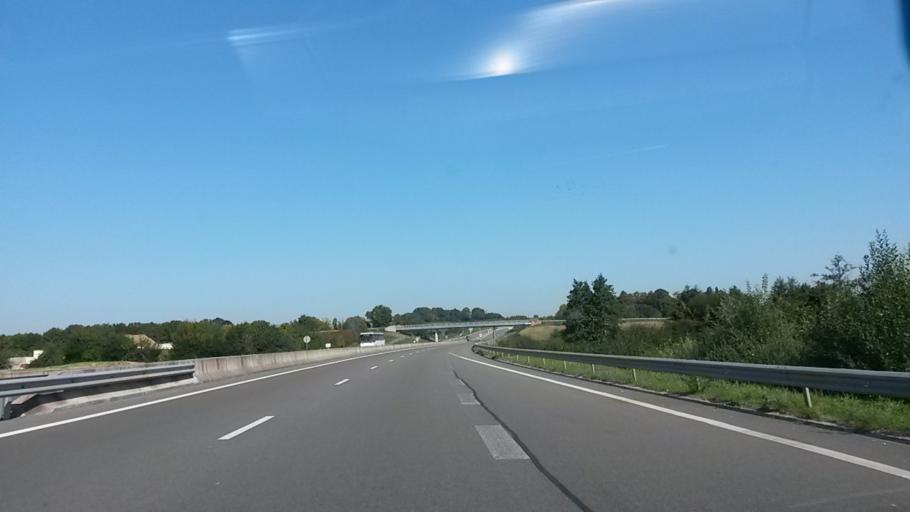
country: FR
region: Nord-Pas-de-Calais
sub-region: Departement du Nord
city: Hautmont
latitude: 50.2085
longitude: 3.9544
